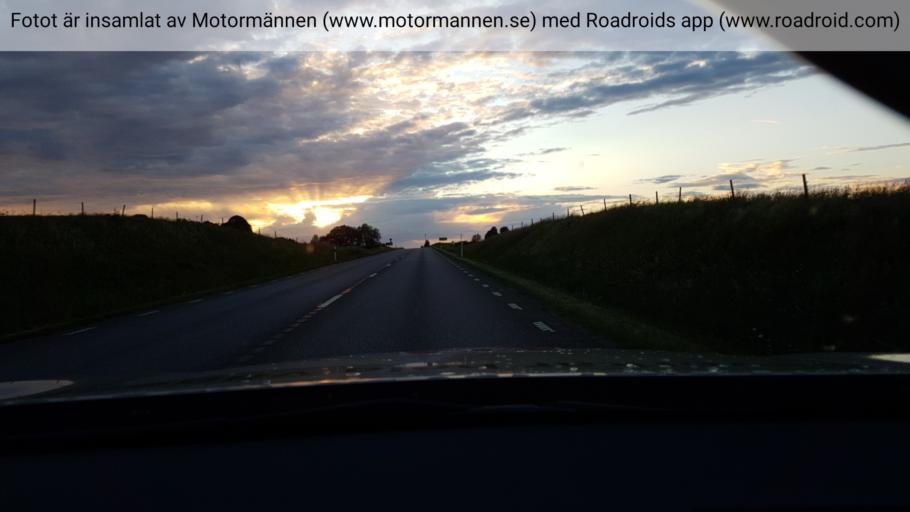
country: SE
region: Vaestra Goetaland
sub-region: Falkopings Kommun
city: Akarp
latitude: 58.0964
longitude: 13.7280
